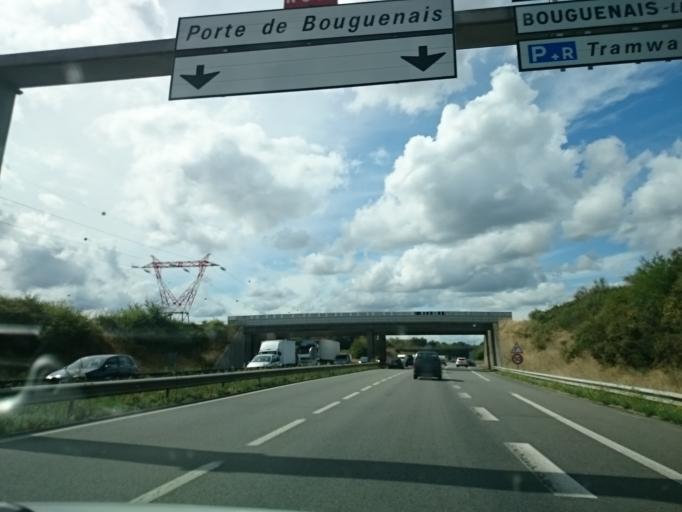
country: FR
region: Pays de la Loire
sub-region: Departement de la Loire-Atlantique
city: Bouguenais
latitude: 47.1717
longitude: -1.5894
